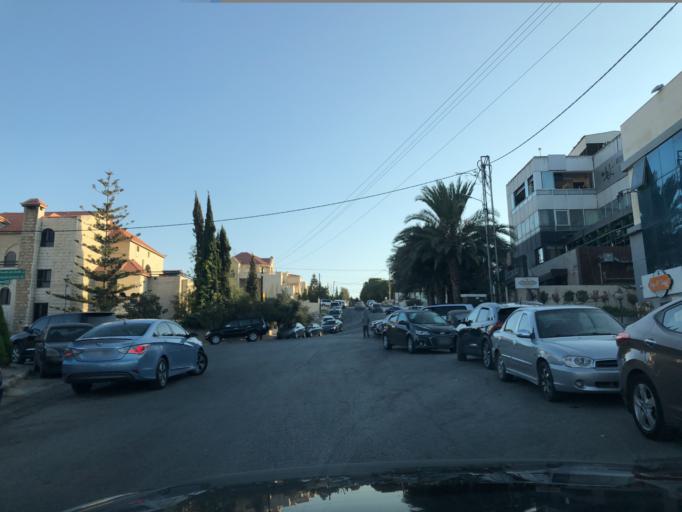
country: JO
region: Amman
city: Al Bunayyat ash Shamaliyah
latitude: 31.9405
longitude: 35.8848
